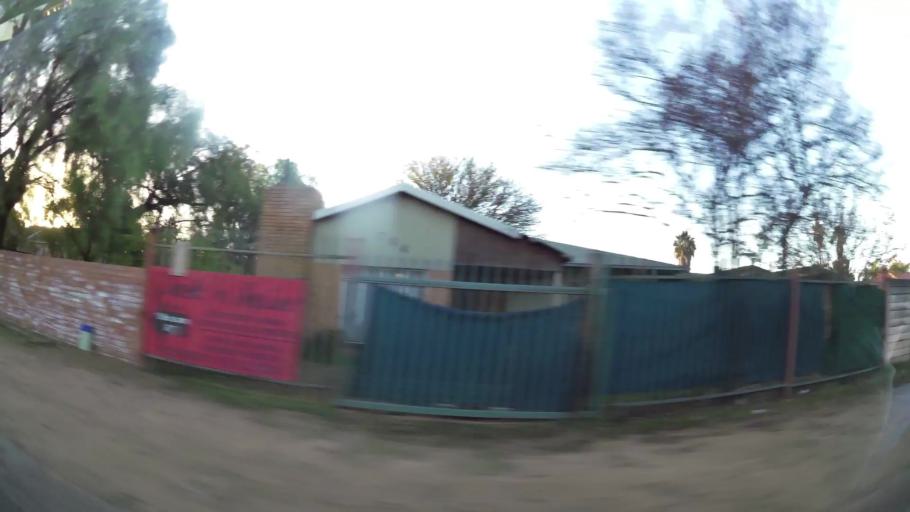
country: ZA
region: Gauteng
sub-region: City of Tshwane Metropolitan Municipality
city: Pretoria
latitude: -25.7122
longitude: 28.2177
